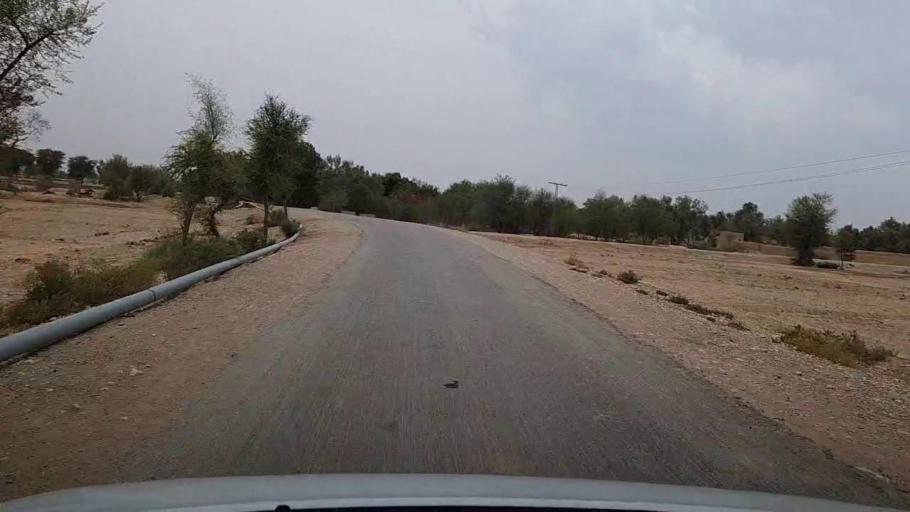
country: PK
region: Sindh
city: Sehwan
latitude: 26.3214
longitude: 67.7313
